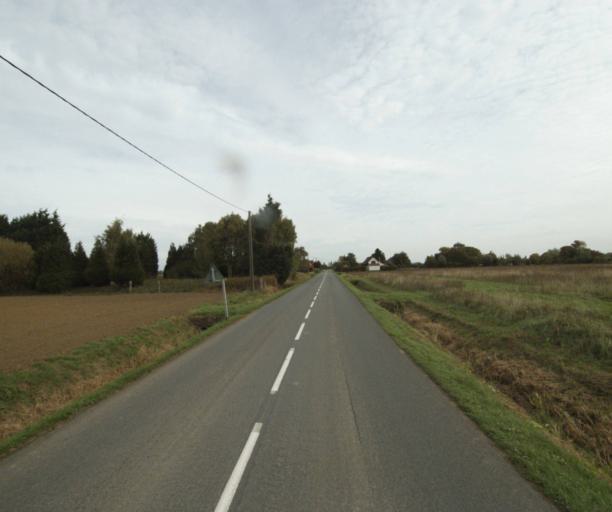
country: FR
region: Nord-Pas-de-Calais
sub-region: Departement du Nord
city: Bois-Grenier
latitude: 50.6216
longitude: 2.8549
